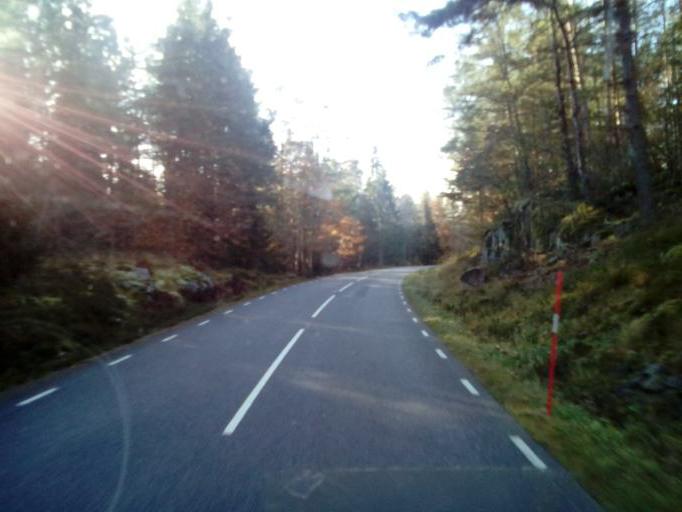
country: SE
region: Kalmar
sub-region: Vasterviks Kommun
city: Ankarsrum
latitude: 57.7552
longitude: 16.1233
